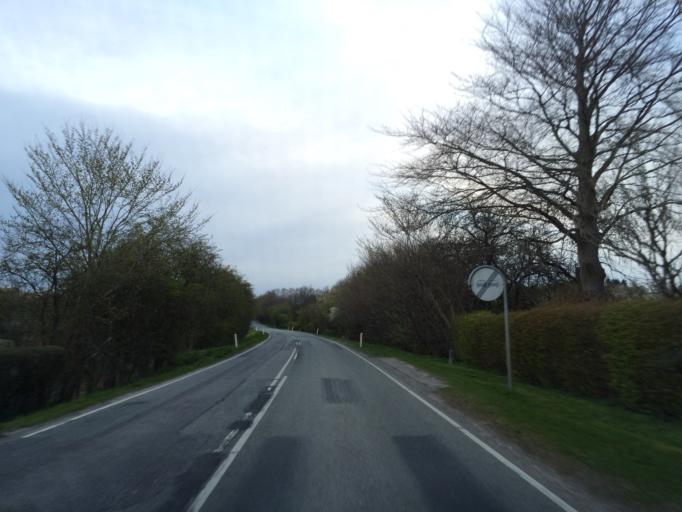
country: DK
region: South Denmark
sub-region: Odense Kommune
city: Bellinge
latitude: 55.3700
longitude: 10.2669
